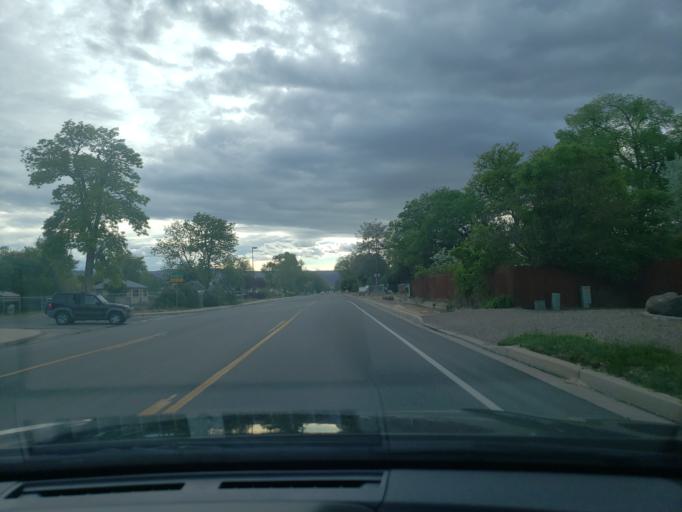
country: US
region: Colorado
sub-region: Mesa County
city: Orchard Mesa
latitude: 39.0484
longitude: -108.5312
